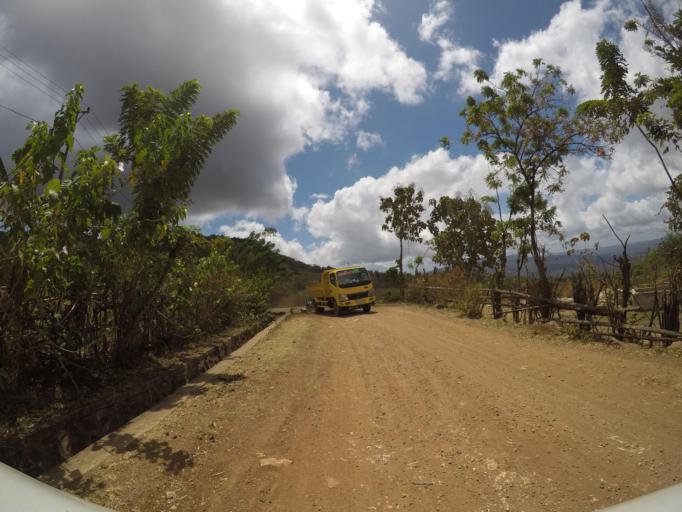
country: TL
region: Lautem
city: Lospalos
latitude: -8.5554
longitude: 126.8293
